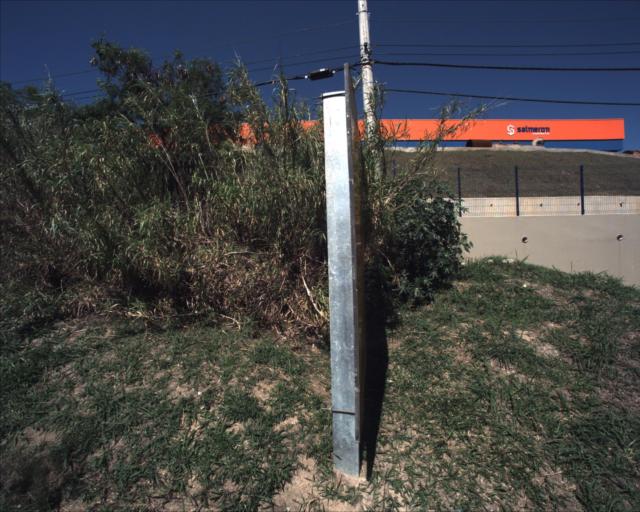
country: BR
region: Sao Paulo
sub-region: Votorantim
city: Votorantim
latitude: -23.5001
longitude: -47.3773
